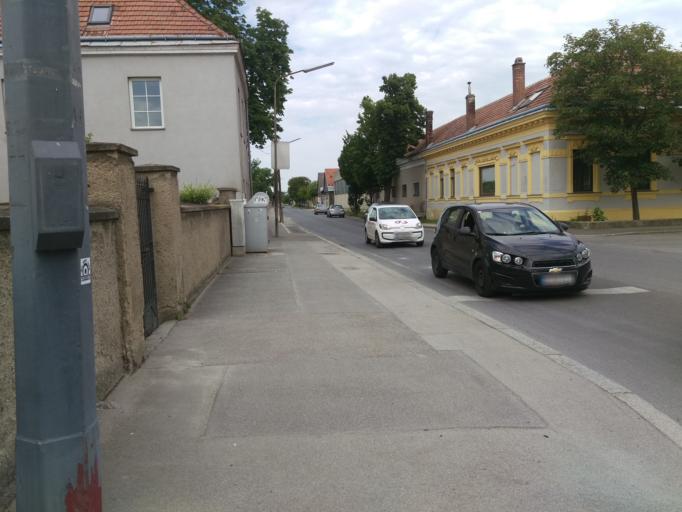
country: AT
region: Lower Austria
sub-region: Politischer Bezirk Ganserndorf
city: Aderklaa
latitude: 48.2513
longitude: 16.4976
